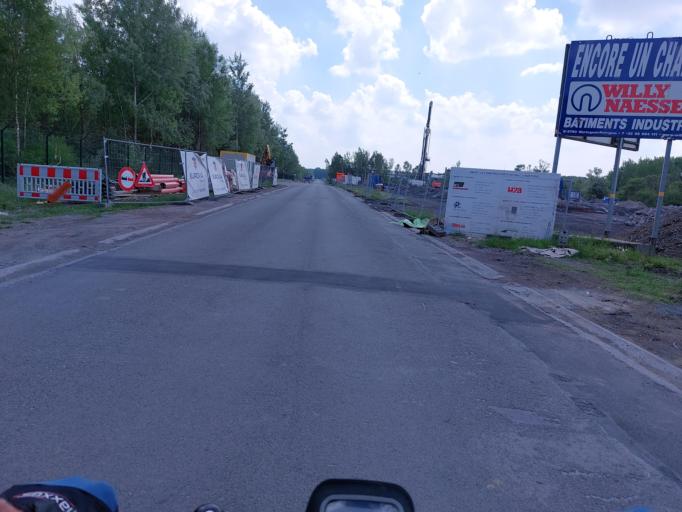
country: BE
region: Wallonia
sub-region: Province du Hainaut
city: Quaregnon
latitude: 50.4687
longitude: 3.8574
